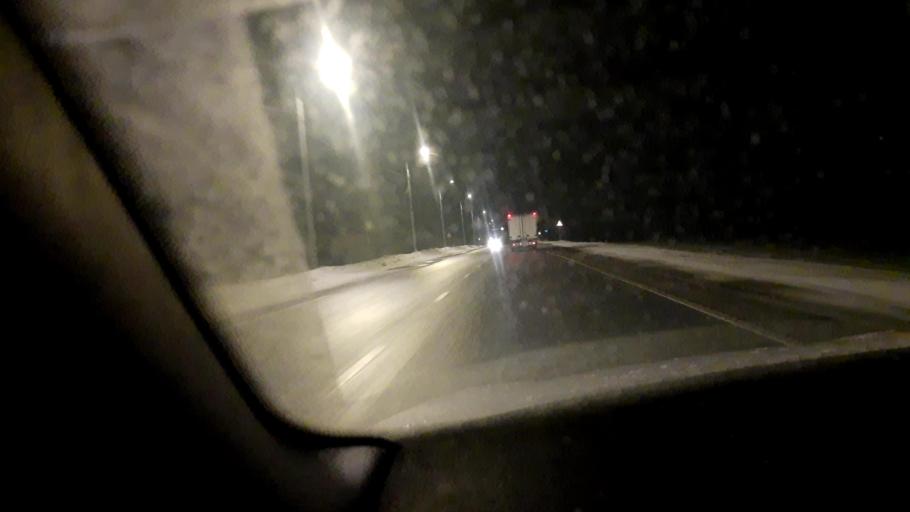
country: RU
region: Moskovskaya
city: Skoropuskovskiy
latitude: 56.3840
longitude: 38.1075
